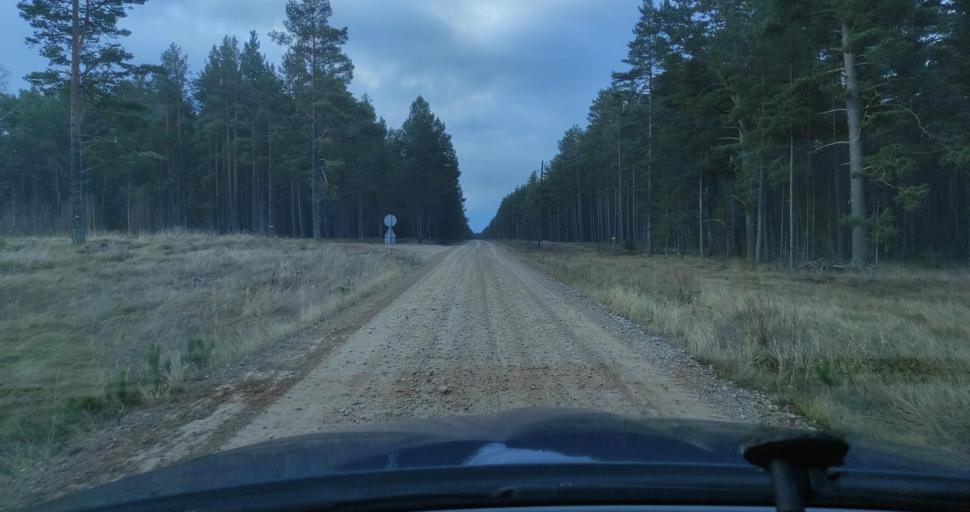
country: LV
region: Pavilostas
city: Pavilosta
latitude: 56.8126
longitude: 21.0653
